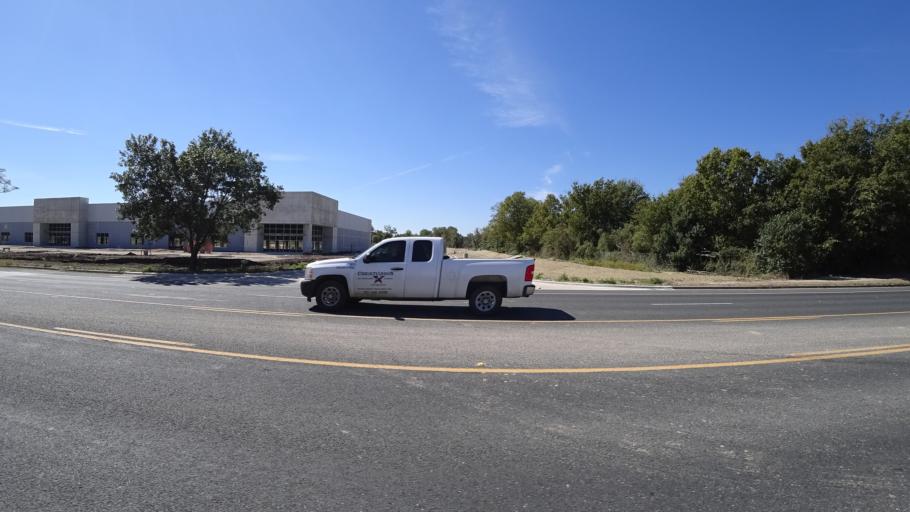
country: US
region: Texas
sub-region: Travis County
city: Austin
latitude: 30.1869
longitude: -97.6927
